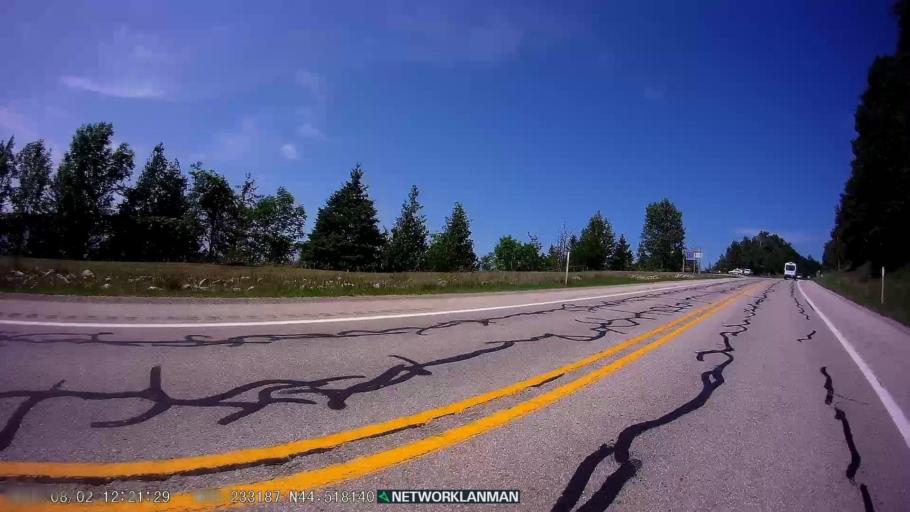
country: US
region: Michigan
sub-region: Benzie County
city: Frankfort
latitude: 44.5184
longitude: -86.2330
